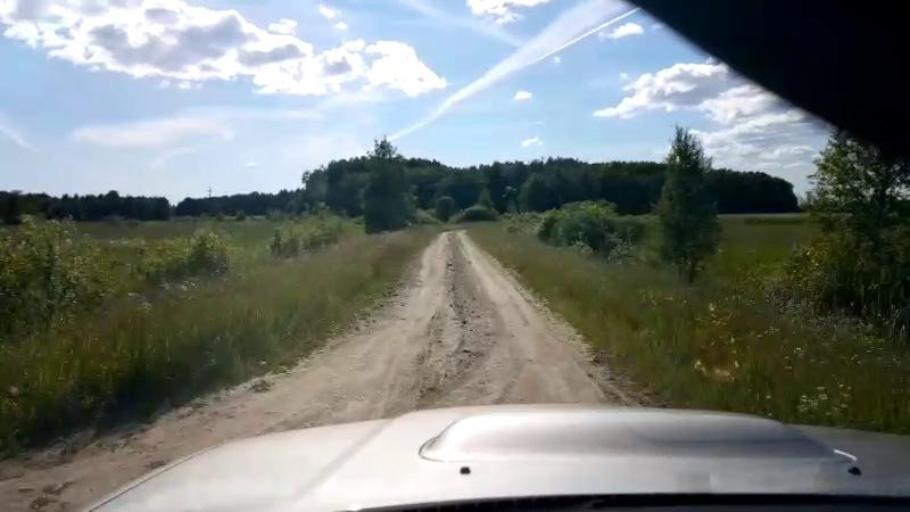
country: EE
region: Paernumaa
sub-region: Sauga vald
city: Sauga
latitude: 58.4920
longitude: 24.5536
